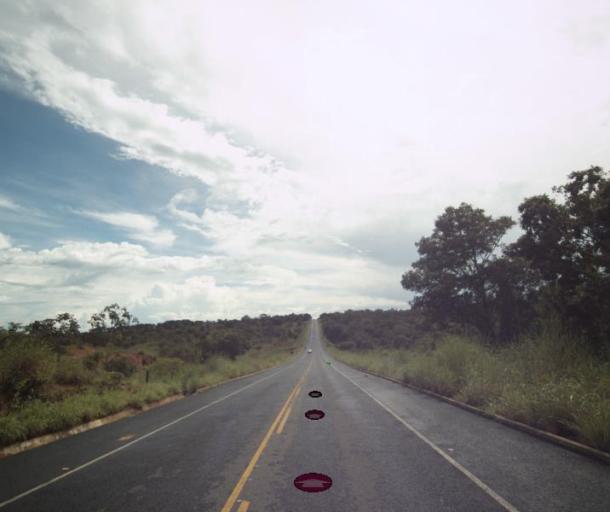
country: BR
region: Goias
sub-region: Sao Miguel Do Araguaia
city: Sao Miguel do Araguaia
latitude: -13.3027
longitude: -50.2717
